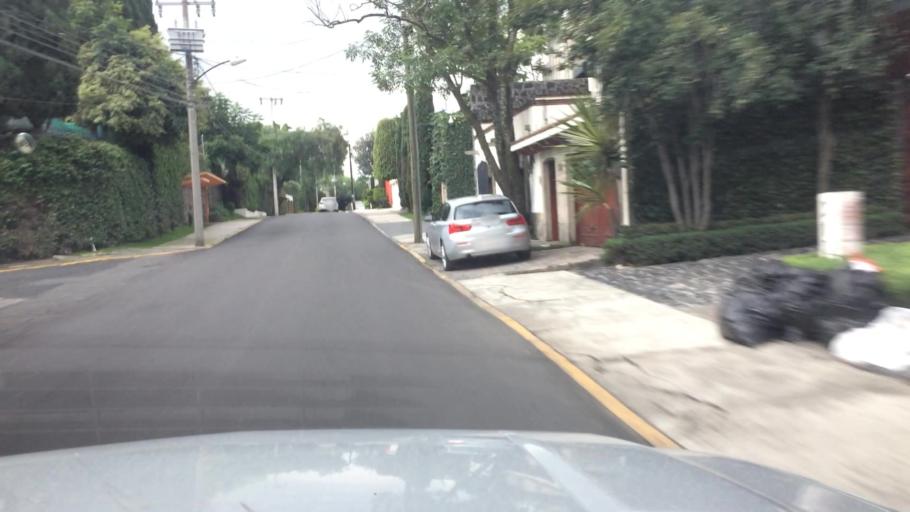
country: MX
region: Mexico City
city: Magdalena Contreras
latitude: 19.3229
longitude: -99.2071
